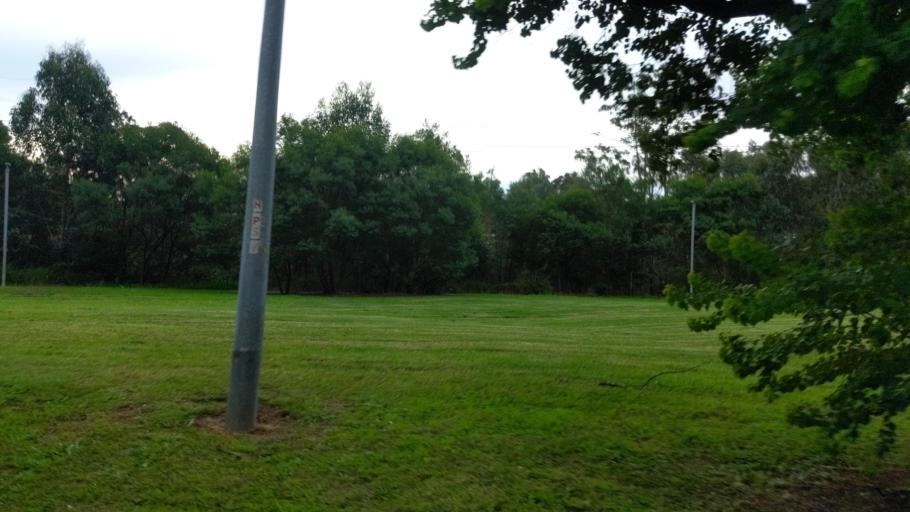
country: AU
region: New South Wales
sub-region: Blacktown
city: Blacktown
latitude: -33.7536
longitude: 150.9460
